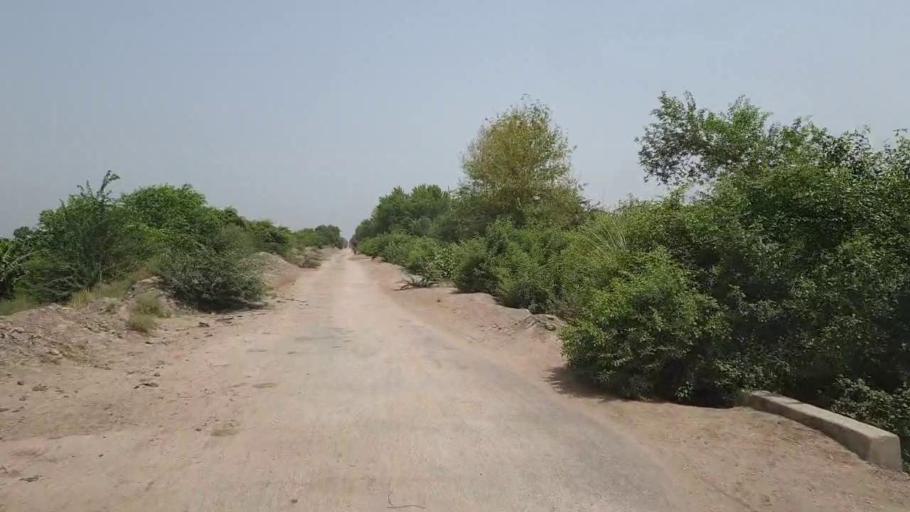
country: PK
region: Sindh
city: Nawabshah
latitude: 26.3051
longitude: 68.3035
